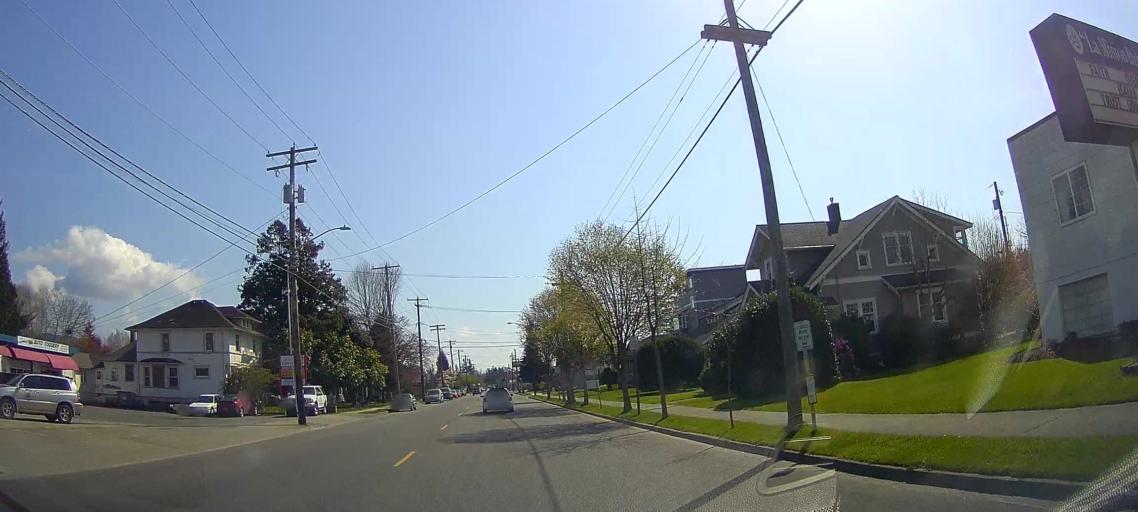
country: US
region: Washington
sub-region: Skagit County
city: Mount Vernon
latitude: 48.4137
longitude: -122.3378
